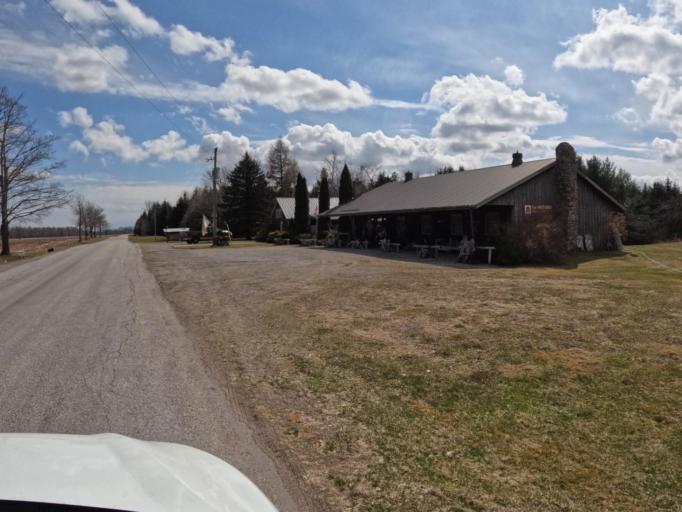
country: CA
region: Ontario
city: Norfolk County
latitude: 42.9060
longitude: -80.1919
